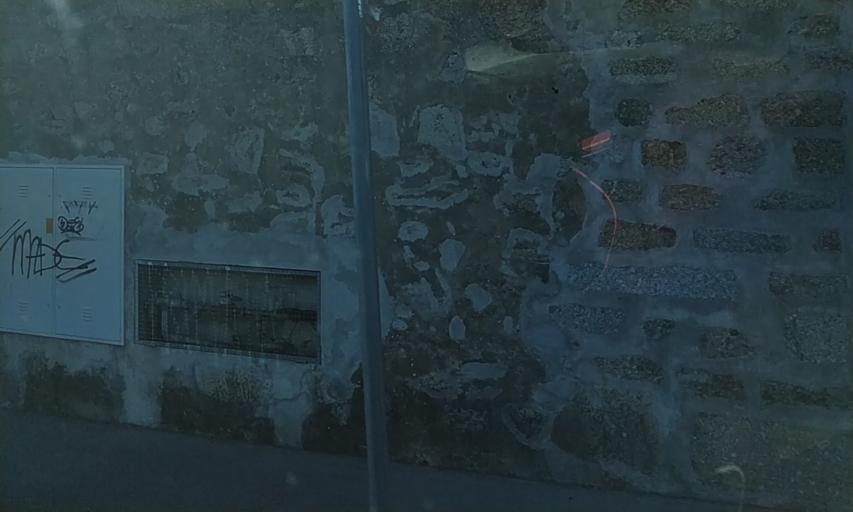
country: PT
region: Porto
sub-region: Santo Tirso
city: Santo Tirso
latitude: 41.3505
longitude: -8.4746
